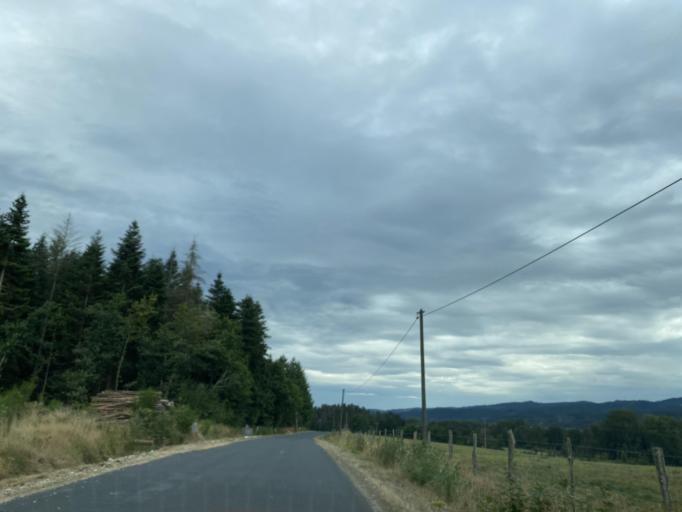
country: FR
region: Auvergne
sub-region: Departement du Puy-de-Dome
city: Marsac-en-Livradois
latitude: 45.5078
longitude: 3.7426
